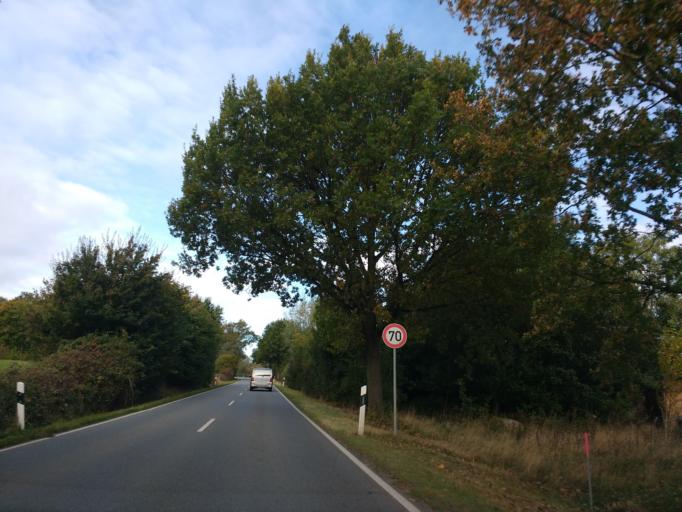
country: DE
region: Schleswig-Holstein
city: Schonwalde am Bungsberg
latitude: 54.1838
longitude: 10.7659
